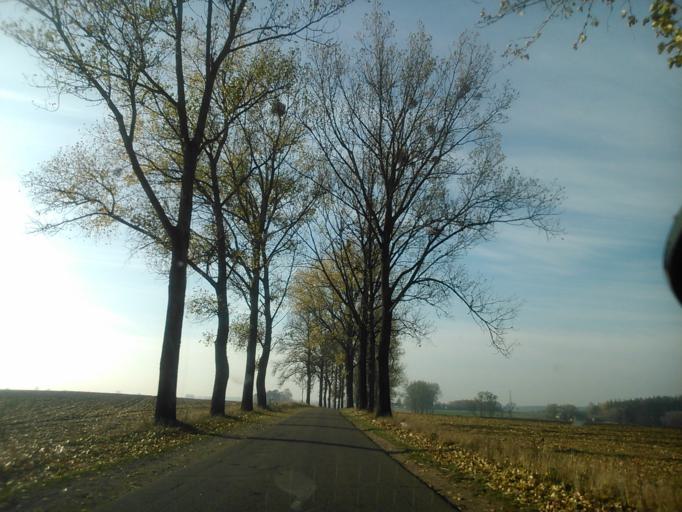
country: PL
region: Warmian-Masurian Voivodeship
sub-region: Powiat dzialdowski
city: Rybno
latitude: 53.2738
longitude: 19.9936
